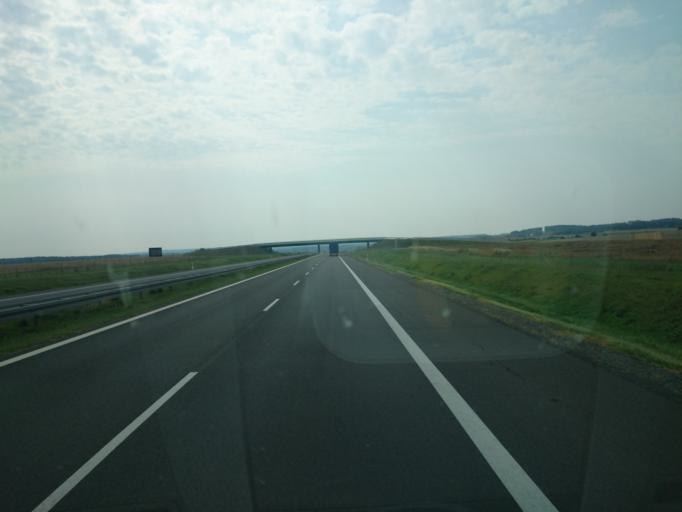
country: PL
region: Lubusz
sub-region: Powiat miedzyrzecki
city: Miedzyrzecz
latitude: 52.3616
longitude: 15.5505
